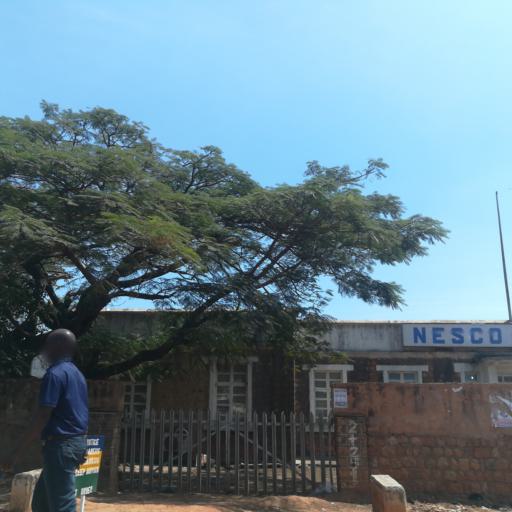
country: NG
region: Plateau
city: Bukuru
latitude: 9.7933
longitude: 8.8651
